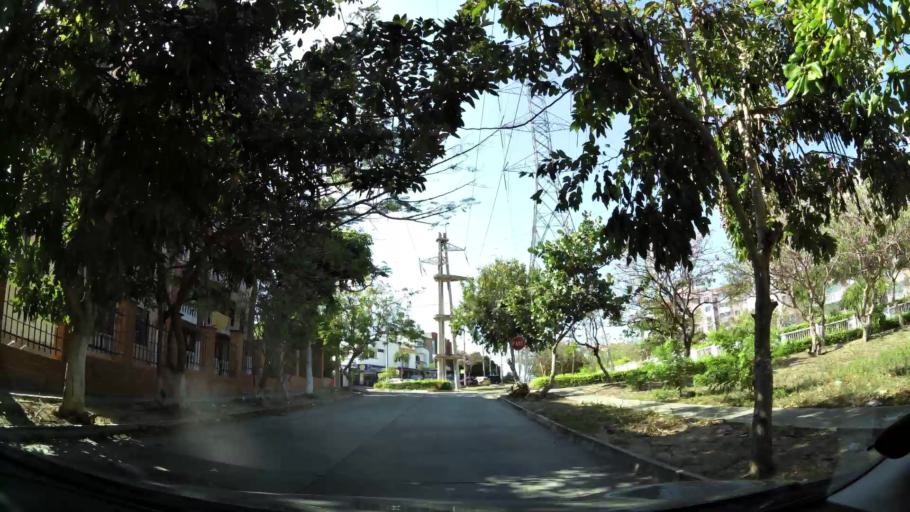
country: CO
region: Atlantico
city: Barranquilla
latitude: 11.0230
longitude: -74.8117
